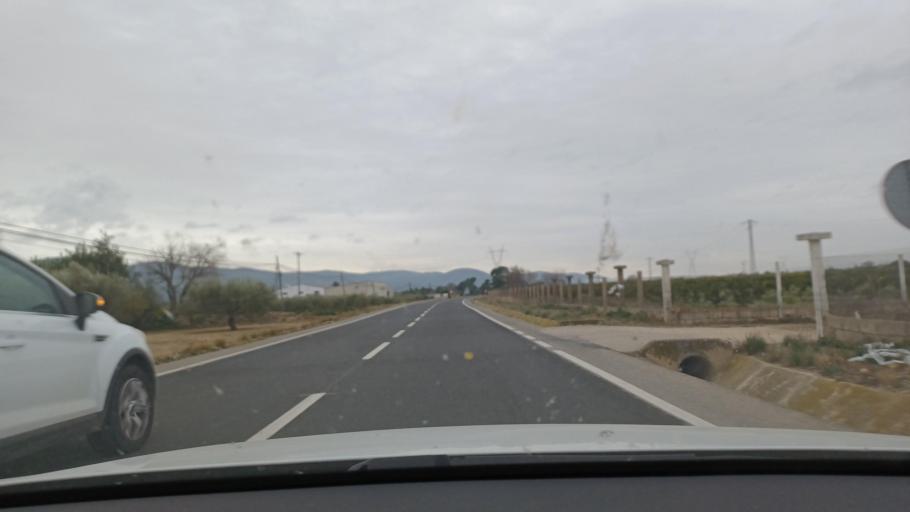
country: ES
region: Catalonia
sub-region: Provincia de Tarragona
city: Santa Barbara
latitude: 40.6972
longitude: 0.4761
